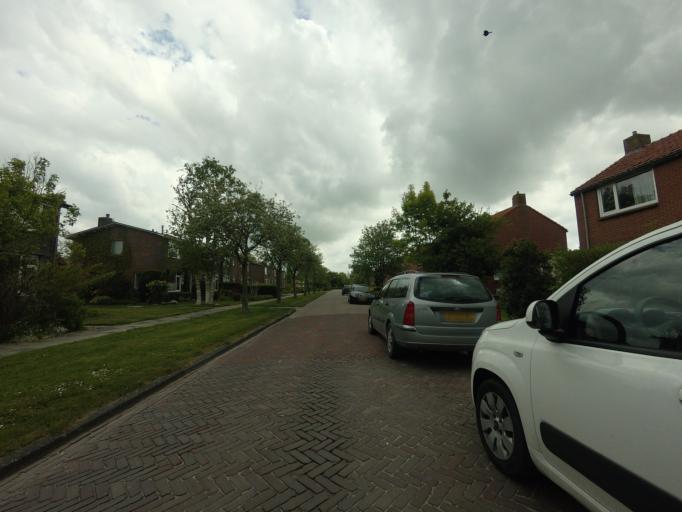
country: NL
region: Friesland
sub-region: Gemeente Littenseradiel
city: Wommels
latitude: 53.1079
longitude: 5.5910
